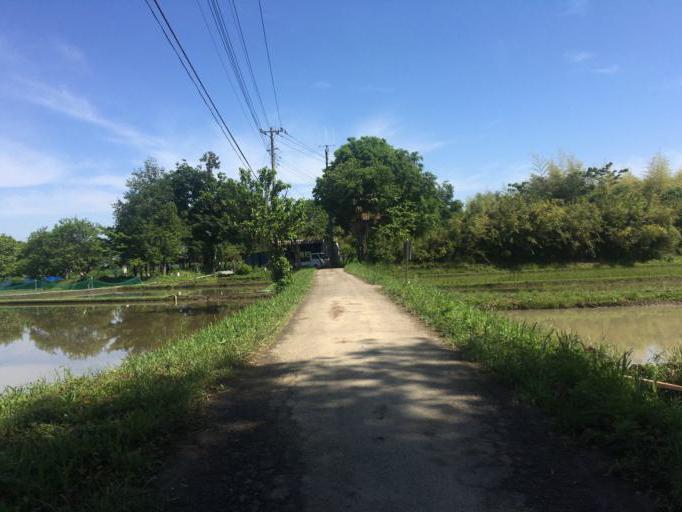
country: JP
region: Saitama
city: Shiki
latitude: 35.8627
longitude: 139.5896
